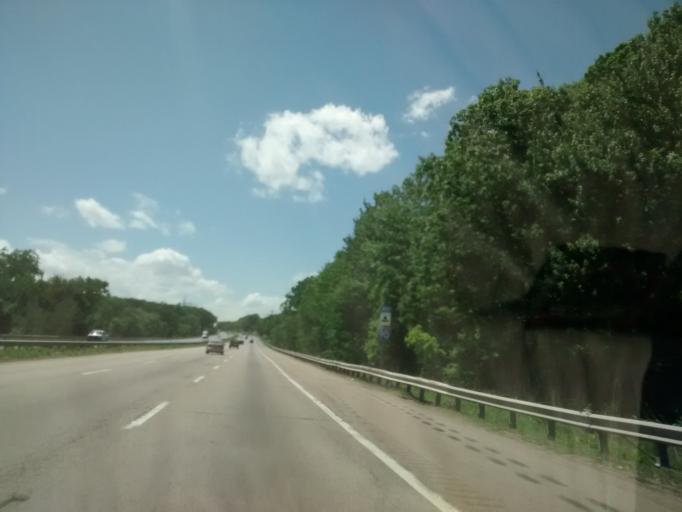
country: US
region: Massachusetts
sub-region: Worcester County
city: Millbury
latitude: 42.2064
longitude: -71.7947
